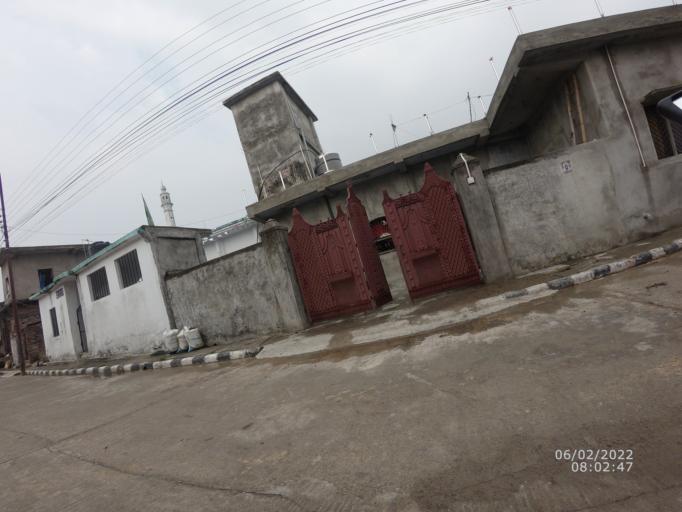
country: NP
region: Western Region
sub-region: Lumbini Zone
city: Bhairahawa
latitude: 27.4800
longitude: 83.4750
